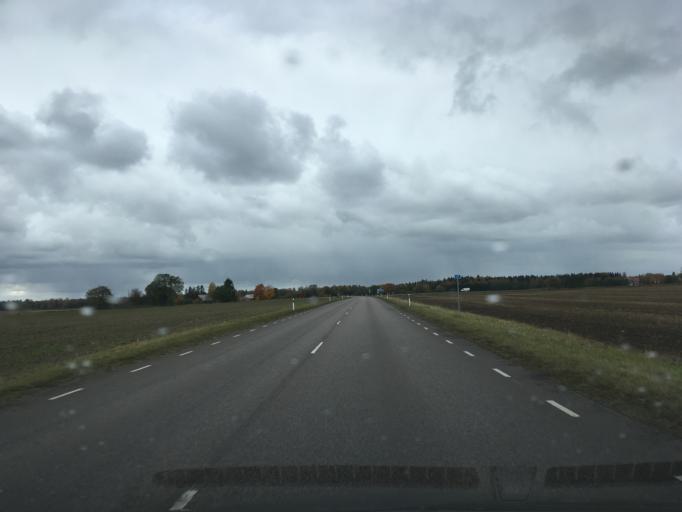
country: EE
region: Harju
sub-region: Anija vald
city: Kehra
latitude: 59.3271
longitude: 25.3263
